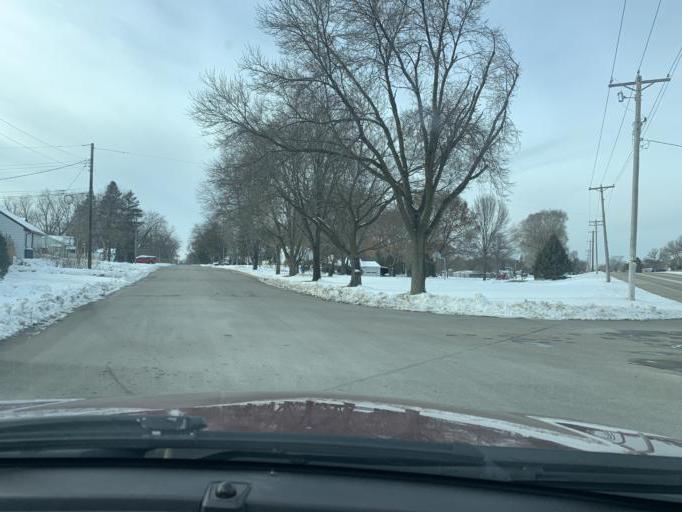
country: US
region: Minnesota
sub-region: Washington County
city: Saint Paul Park
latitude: 44.8403
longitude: -92.9789
